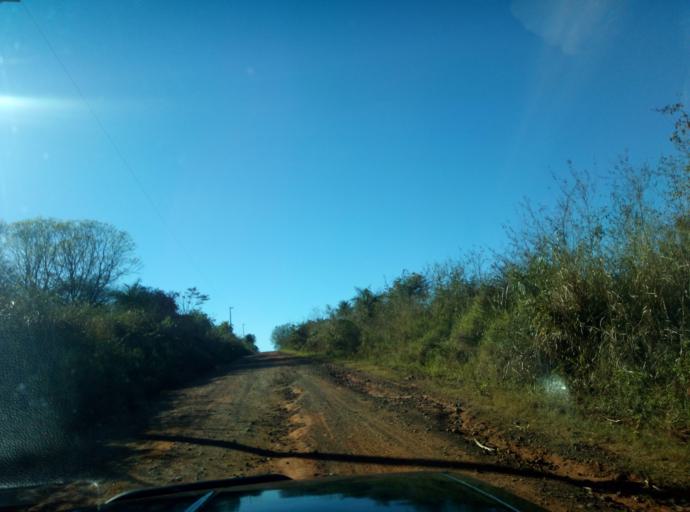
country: PY
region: Caaguazu
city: Carayao
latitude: -25.1580
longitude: -56.2951
